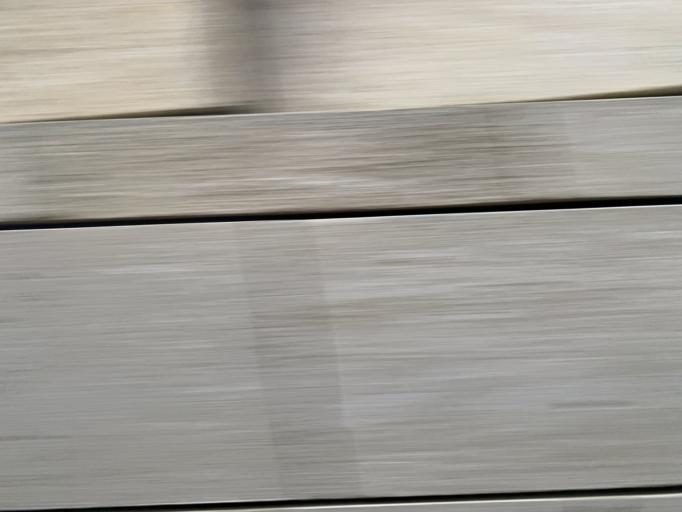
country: FR
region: Rhone-Alpes
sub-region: Departement du Rhone
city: Meyzieu
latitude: 45.7708
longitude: 5.0057
